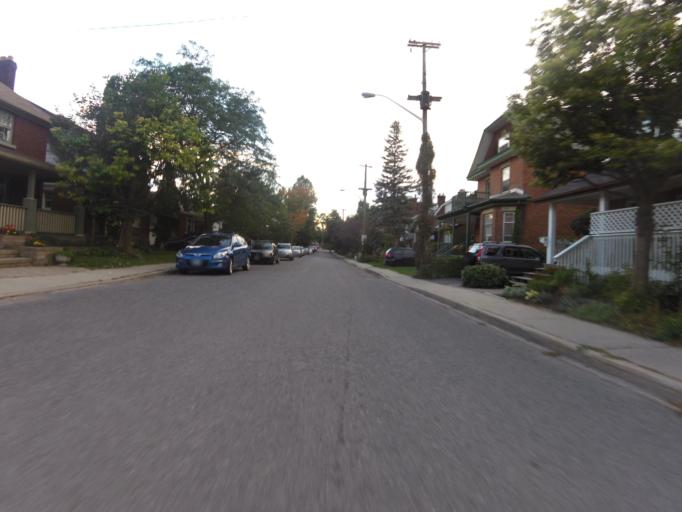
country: CA
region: Ontario
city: Ottawa
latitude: 45.3969
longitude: -75.6770
